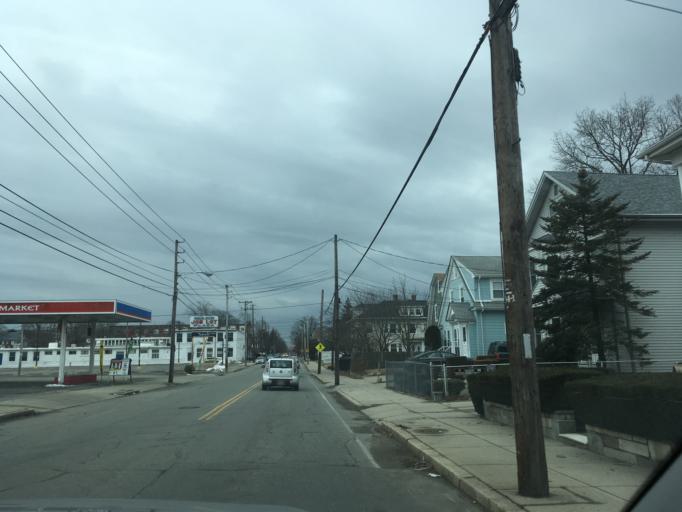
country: US
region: Rhode Island
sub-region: Providence County
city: Pawtucket
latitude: 41.8630
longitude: -71.3944
